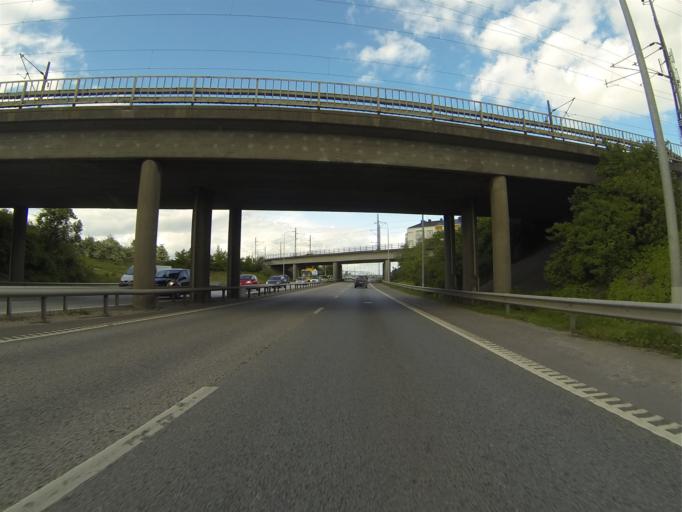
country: SE
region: Skane
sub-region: Malmo
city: Malmoe
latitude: 55.6094
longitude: 13.0286
